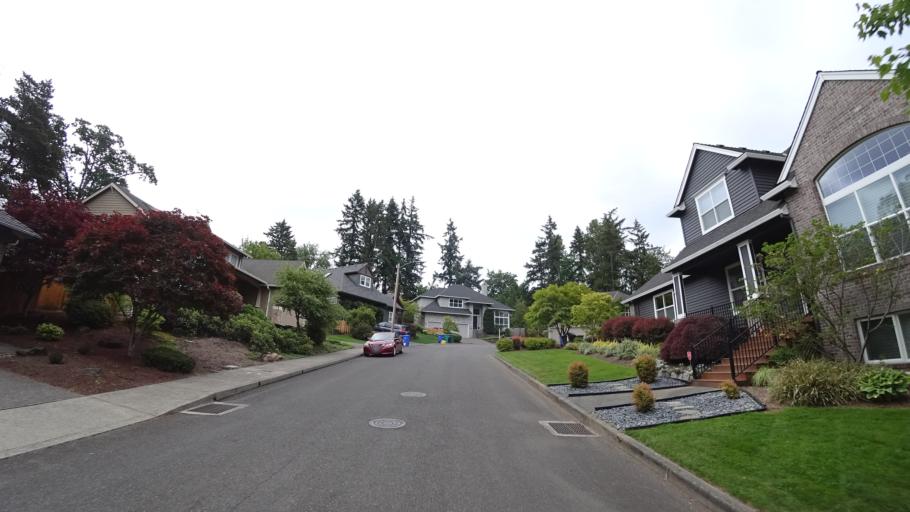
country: US
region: Oregon
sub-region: Washington County
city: Garden Home-Whitford
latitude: 45.4690
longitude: -122.7415
